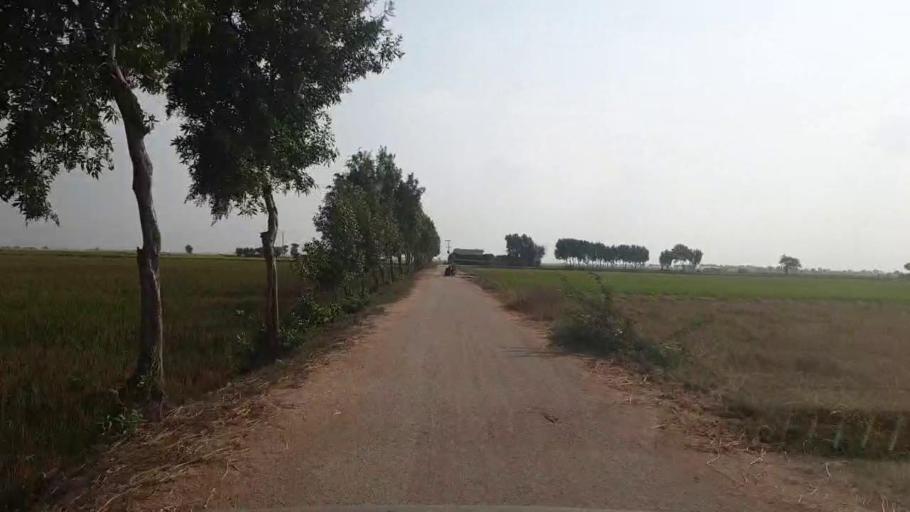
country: PK
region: Sindh
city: Kario
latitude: 24.6365
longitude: 68.5580
